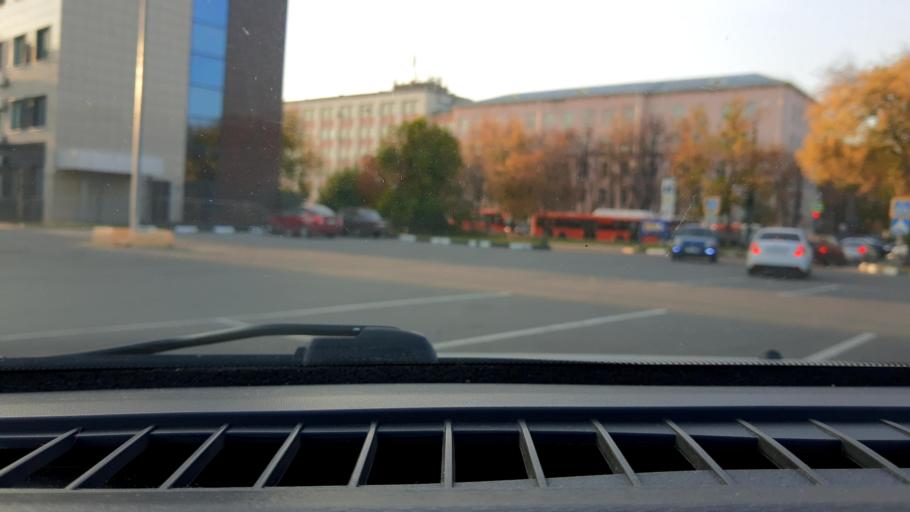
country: RU
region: Nizjnij Novgorod
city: Nizhniy Novgorod
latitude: 56.3172
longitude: 43.9198
